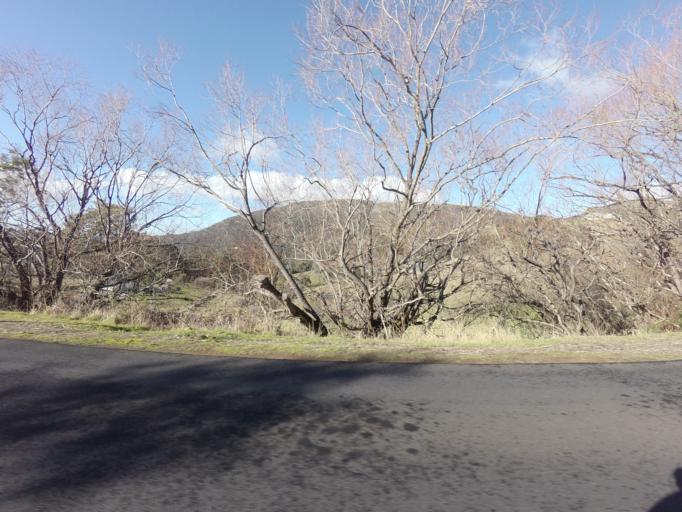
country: AU
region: Tasmania
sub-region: Glenorchy
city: Berriedale
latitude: -42.8256
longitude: 147.2003
